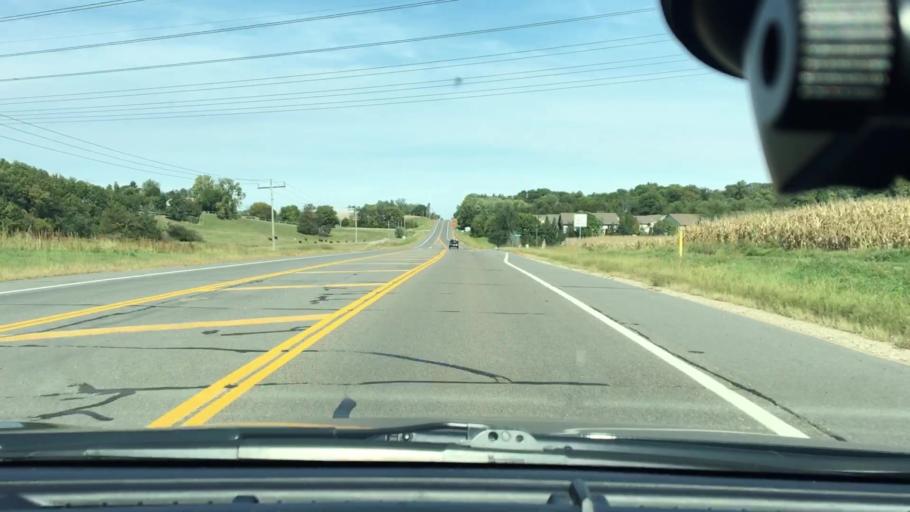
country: US
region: Minnesota
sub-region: Wright County
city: Hanover
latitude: 45.1762
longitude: -93.6656
